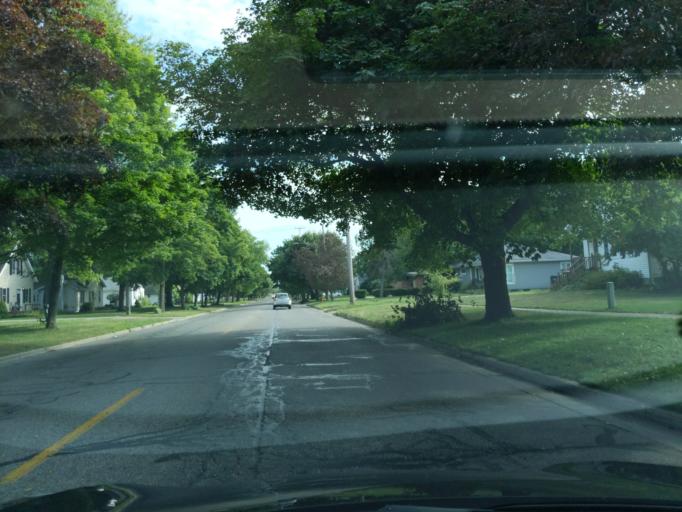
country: US
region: Michigan
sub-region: Midland County
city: Midland
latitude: 43.6382
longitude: -84.2270
